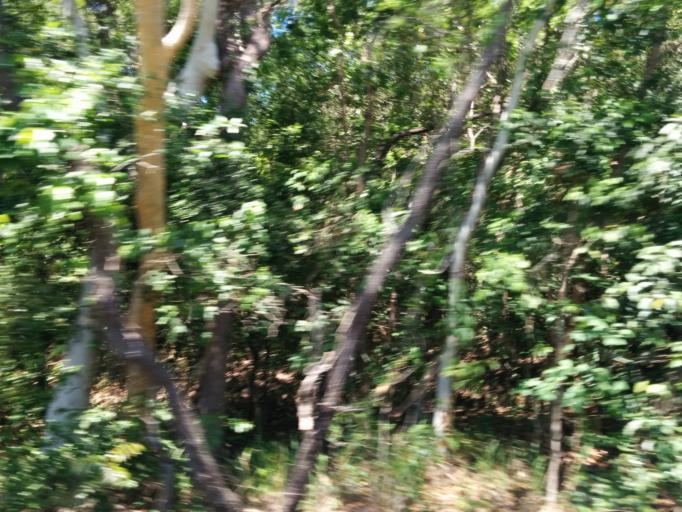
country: AU
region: Queensland
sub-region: Cairns
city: Palm Cove
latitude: -16.6785
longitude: 145.5724
